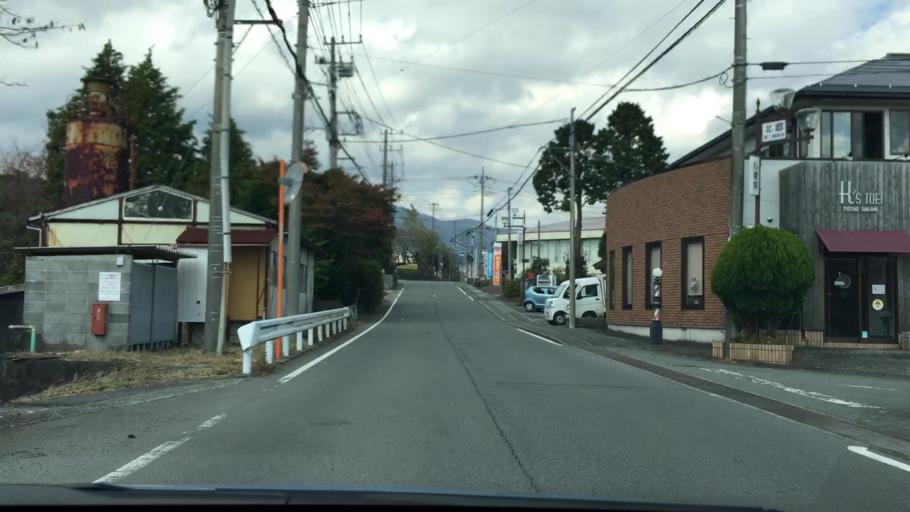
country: JP
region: Shizuoka
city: Gotemba
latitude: 35.3431
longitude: 138.9443
